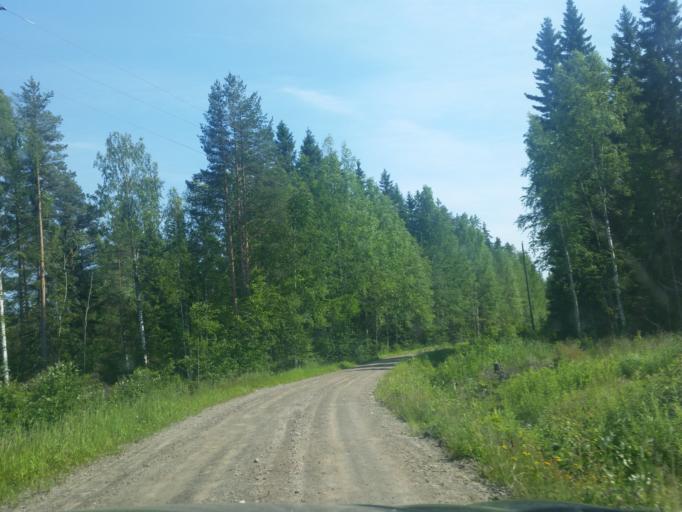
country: FI
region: Northern Savo
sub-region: Ylae-Savo
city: Keitele
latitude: 63.0975
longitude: 26.5704
